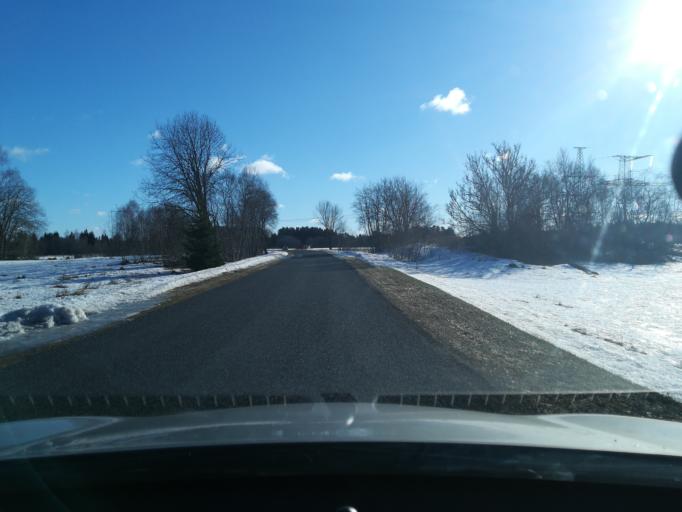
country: EE
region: Raplamaa
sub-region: Kohila vald
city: Kohila
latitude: 59.2368
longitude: 24.7561
